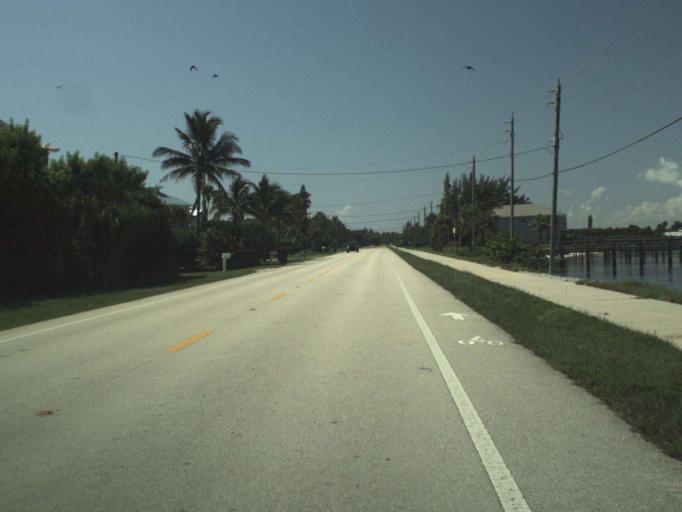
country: US
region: Florida
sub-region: Indian River County
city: Sebastian
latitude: 27.8291
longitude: -80.4321
